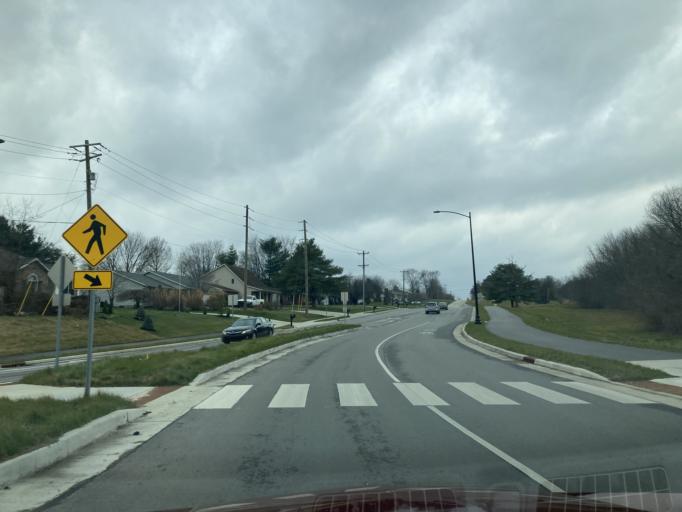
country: US
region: Indiana
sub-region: Monroe County
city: Bloomington
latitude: 39.1217
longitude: -86.5394
